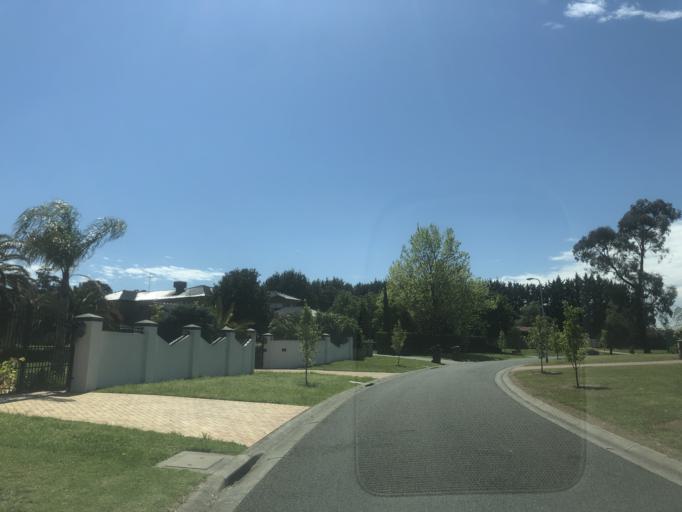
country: AU
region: Victoria
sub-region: Casey
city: Endeavour Hills
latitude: -37.9804
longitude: 145.2855
